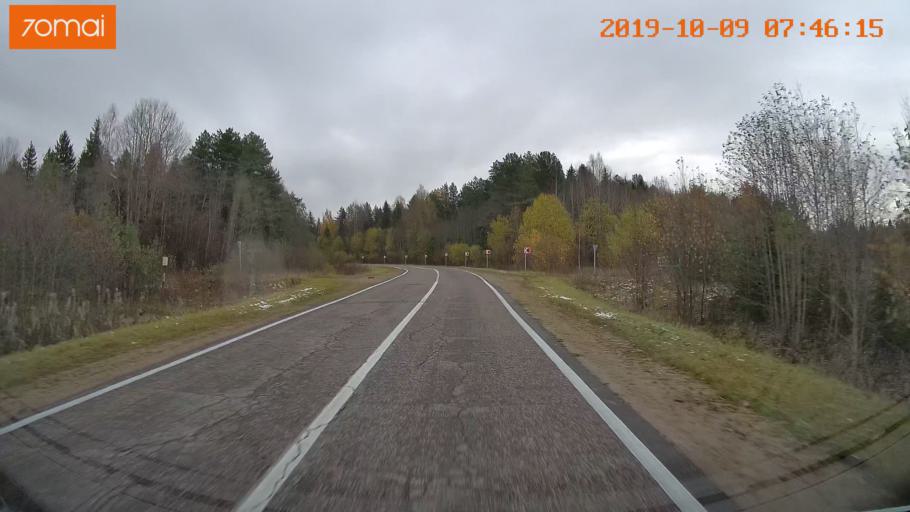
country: RU
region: Jaroslavl
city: Kukoboy
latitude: 58.6556
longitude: 39.7840
